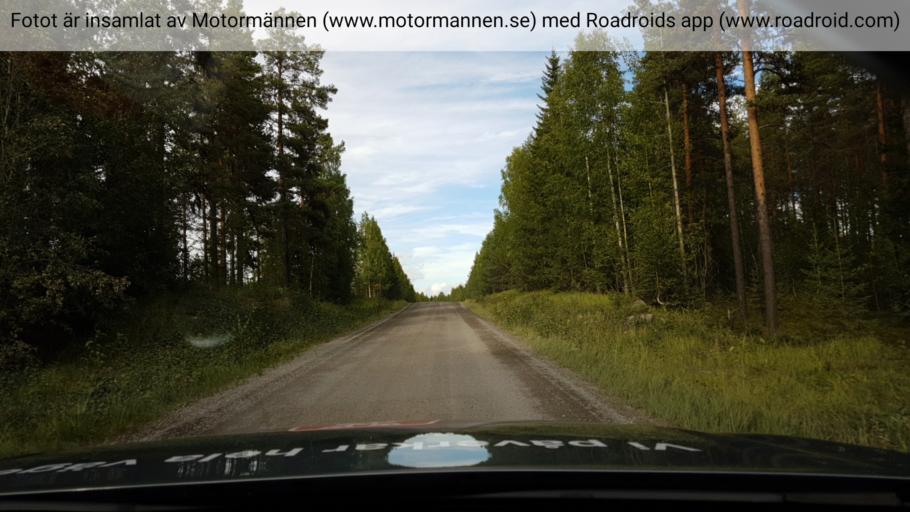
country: SE
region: Jaemtland
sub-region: Braecke Kommun
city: Braecke
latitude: 63.2298
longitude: 15.3538
